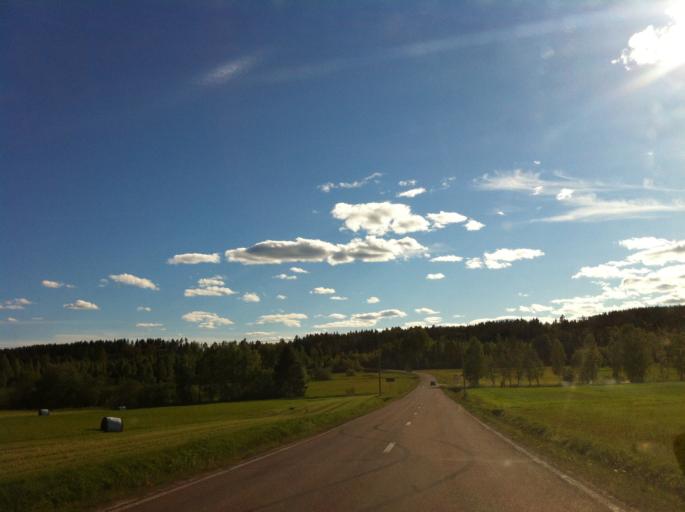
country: SE
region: Dalarna
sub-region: Leksand Municipality
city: Siljansnas
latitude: 60.7735
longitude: 14.8454
